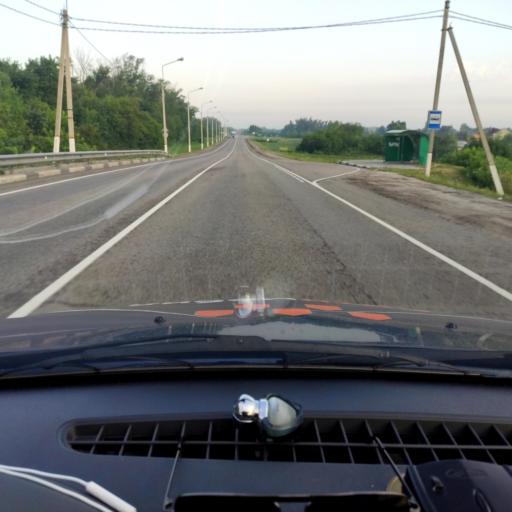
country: RU
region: Lipetsk
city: Yelets
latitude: 52.5582
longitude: 38.6933
